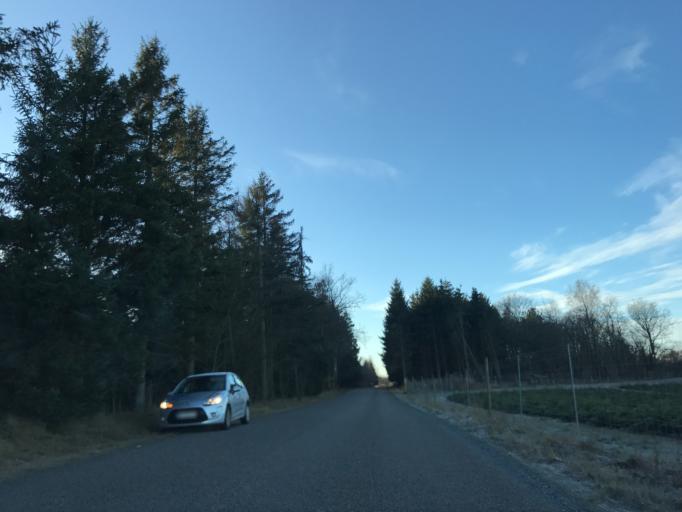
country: DK
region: Central Jutland
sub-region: Silkeborg Kommune
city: Svejbaek
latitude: 56.1644
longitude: 9.6531
